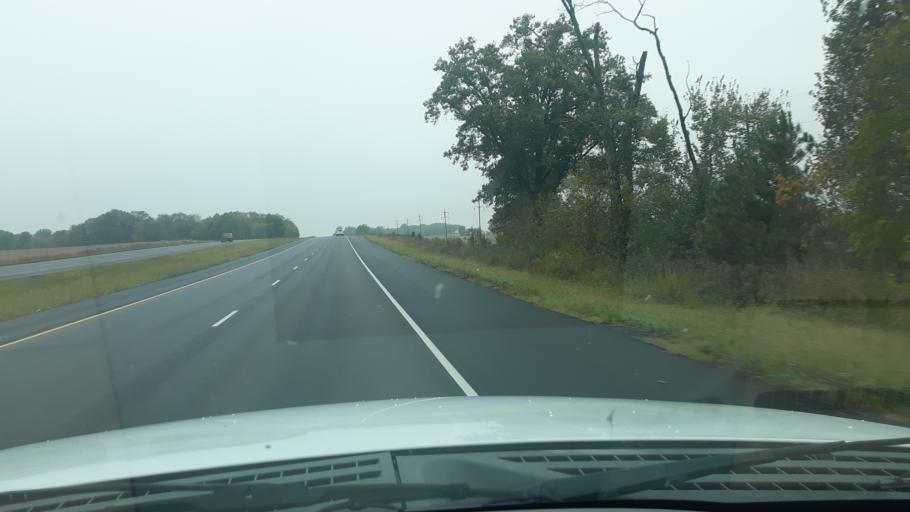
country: US
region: Illinois
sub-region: Saline County
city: Eldorado
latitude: 37.7959
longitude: -88.4703
